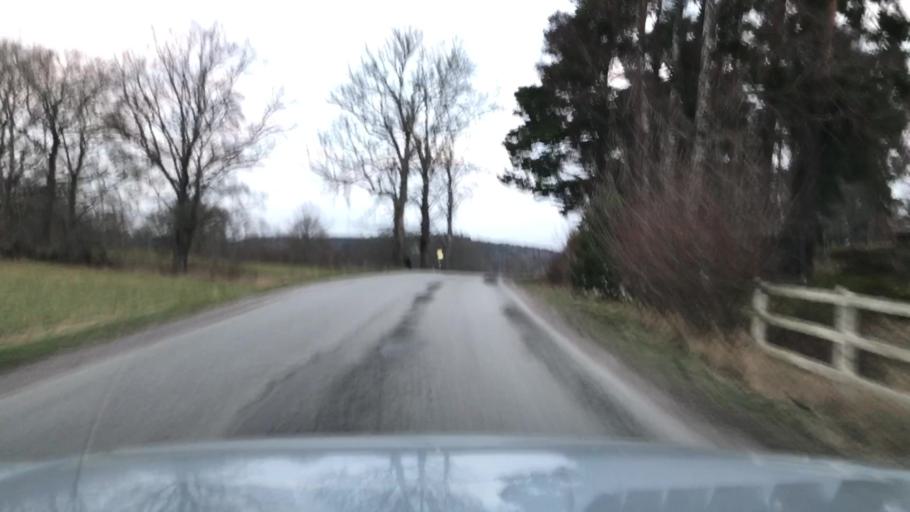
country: SE
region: OEstergoetland
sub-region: Norrkopings Kommun
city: Kimstad
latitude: 58.5199
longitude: 15.9724
